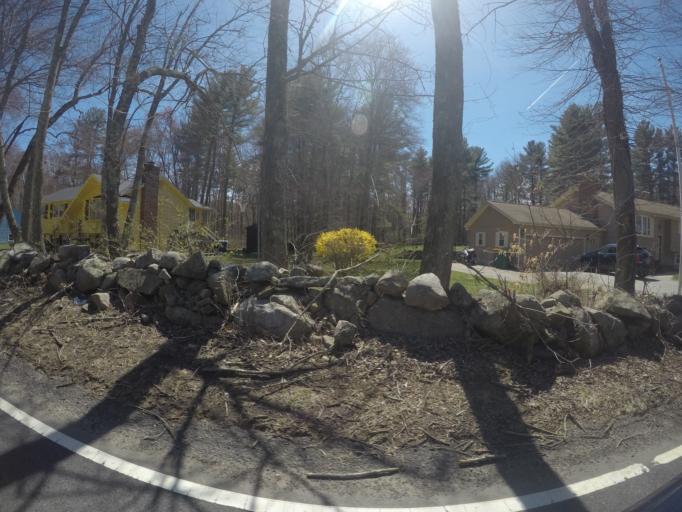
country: US
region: Massachusetts
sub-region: Bristol County
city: Easton
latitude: 42.0439
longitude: -71.0946
